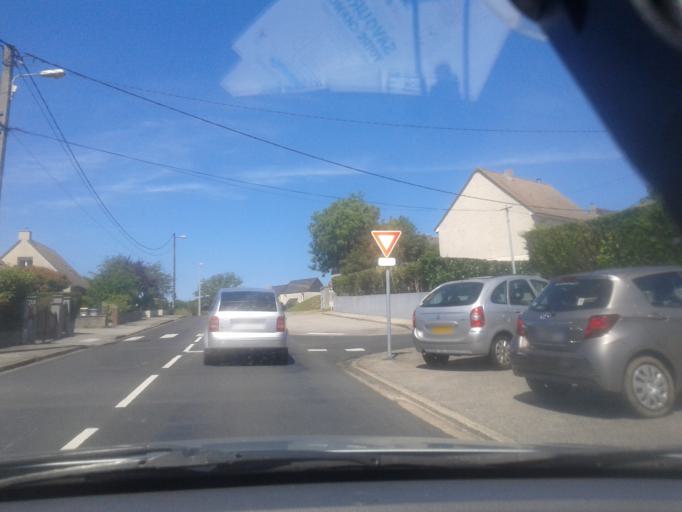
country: FR
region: Lower Normandy
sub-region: Departement de la Manche
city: Equeurdreville-Hainneville
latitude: 49.6482
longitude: -1.6680
